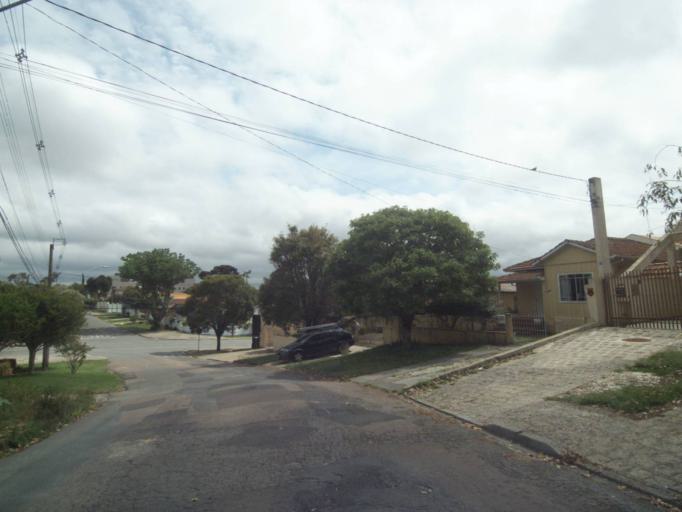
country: BR
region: Parana
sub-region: Pinhais
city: Pinhais
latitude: -25.4379
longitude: -49.2311
